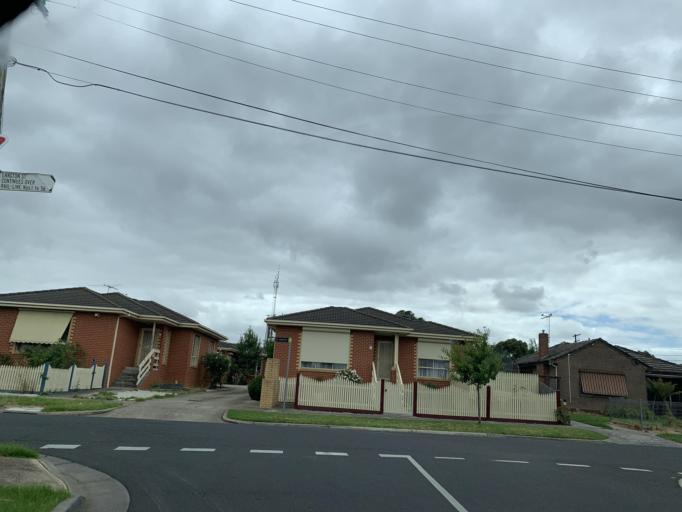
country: AU
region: Victoria
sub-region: Hume
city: Jacana
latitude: -37.6965
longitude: 144.9138
